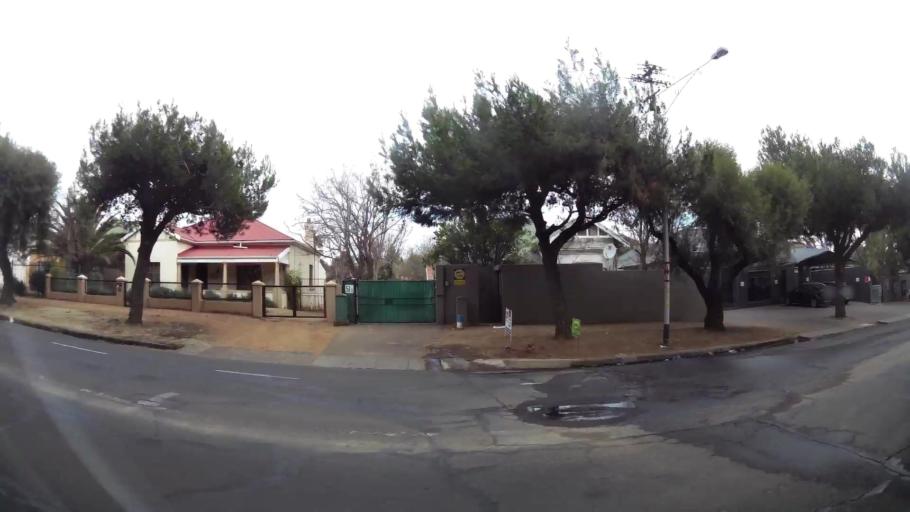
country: ZA
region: Orange Free State
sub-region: Mangaung Metropolitan Municipality
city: Bloemfontein
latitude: -29.1036
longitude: 26.2085
